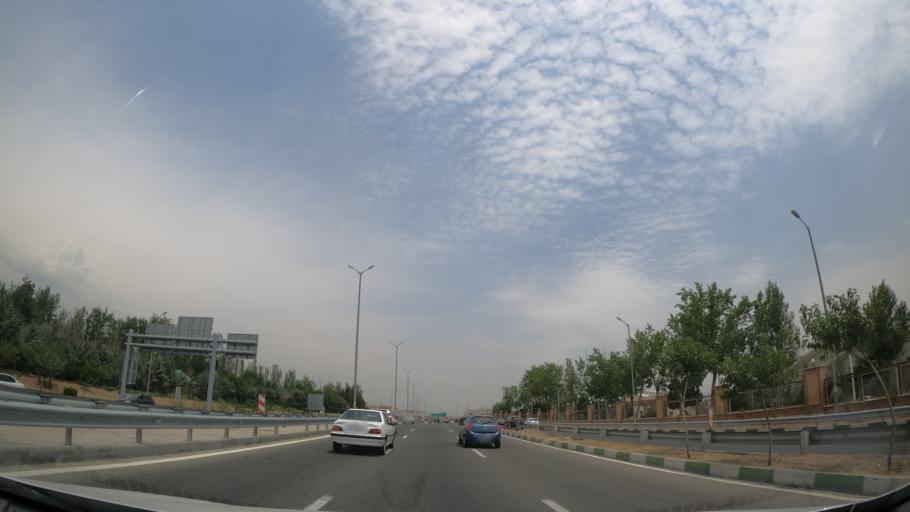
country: IR
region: Tehran
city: Shahr-e Qods
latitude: 35.7388
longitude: 51.2581
